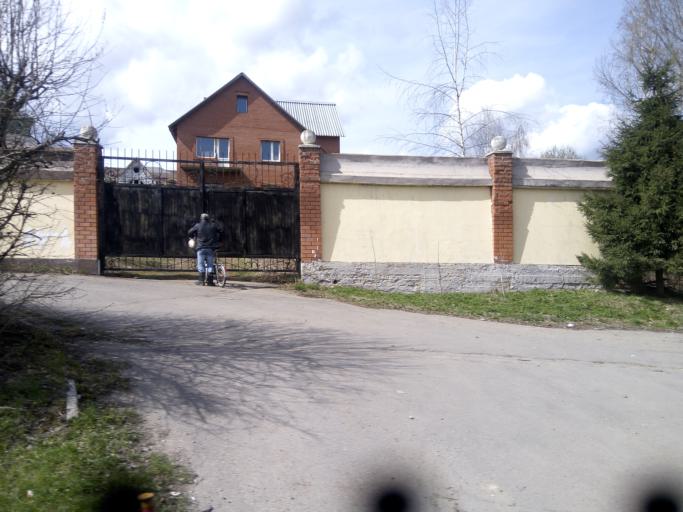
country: RU
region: Moskovskaya
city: Skolkovo
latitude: 55.6833
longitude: 37.3668
